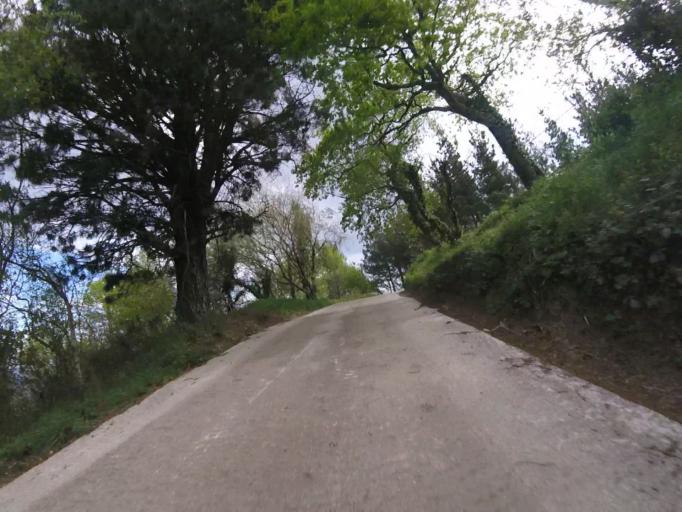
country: ES
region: Basque Country
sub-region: Provincia de Guipuzcoa
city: Zarautz
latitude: 43.2515
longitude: -2.1830
